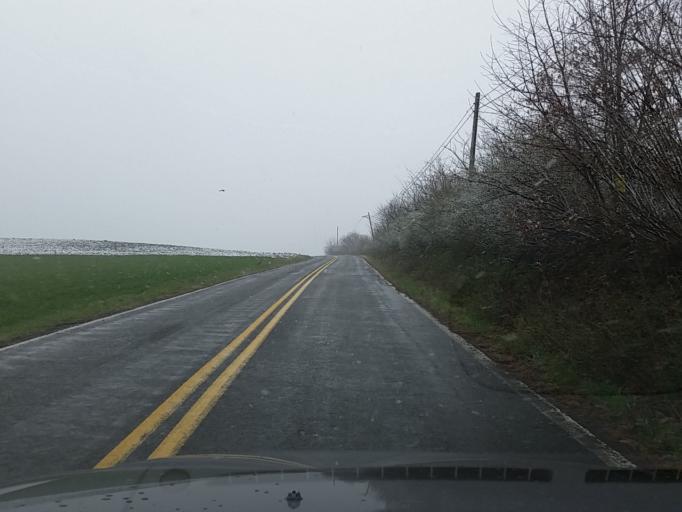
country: US
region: Pennsylvania
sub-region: Luzerne County
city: Glen Lyon
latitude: 41.1989
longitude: -76.1946
